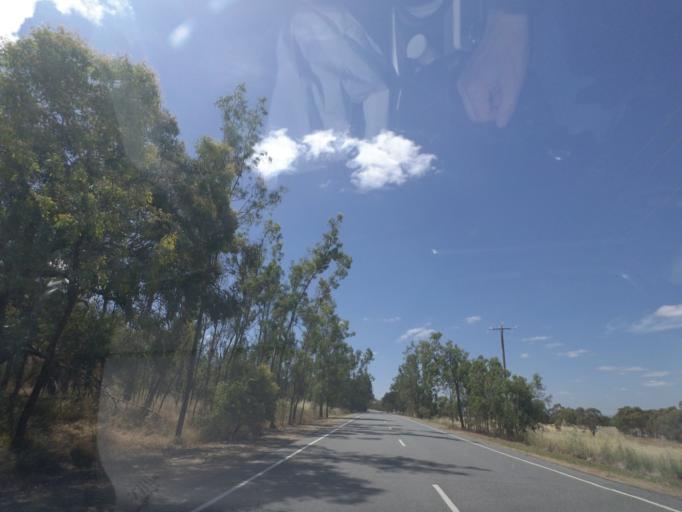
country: AU
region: Victoria
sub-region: Wangaratta
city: Wangaratta
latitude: -36.4548
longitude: 146.2371
